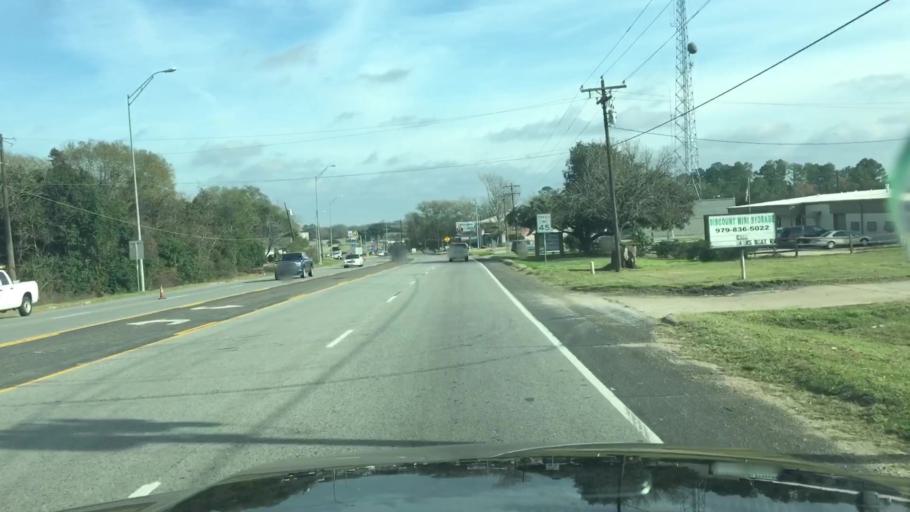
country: US
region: Texas
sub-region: Washington County
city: Brenham
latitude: 30.1671
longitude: -96.4330
